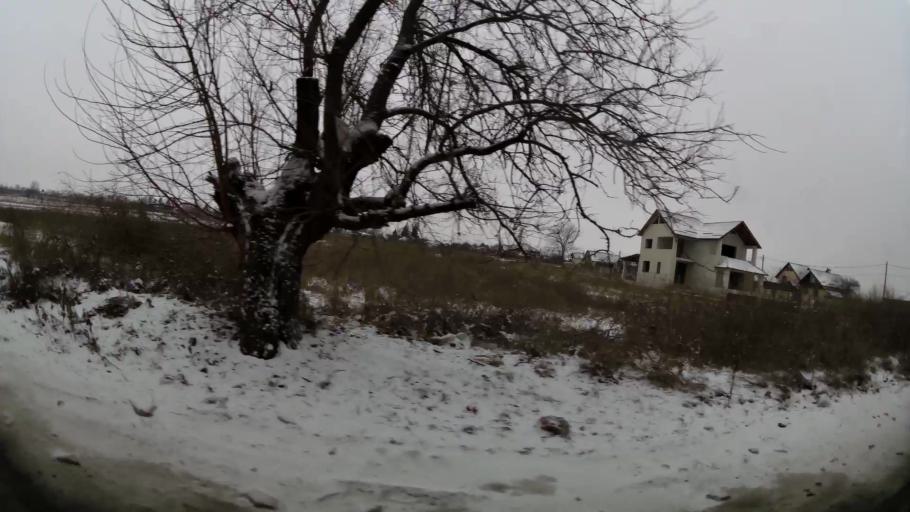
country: RO
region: Dambovita
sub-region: Comuna Ulmi
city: Ulmi
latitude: 44.8999
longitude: 25.5026
